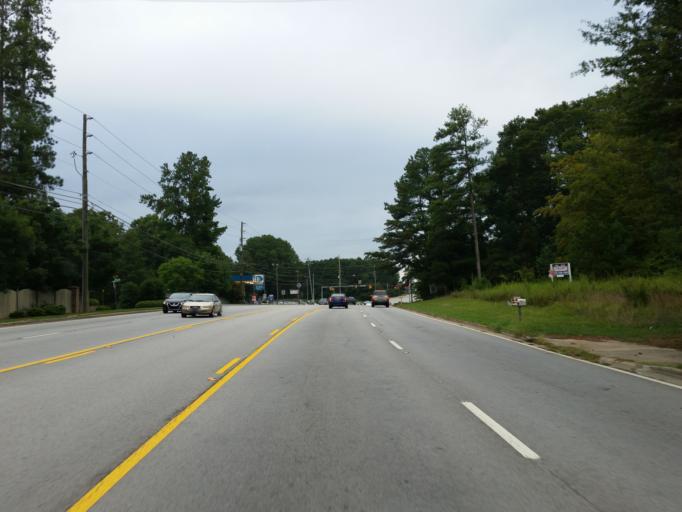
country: US
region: Georgia
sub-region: Cobb County
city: Powder Springs
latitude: 33.8713
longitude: -84.6264
